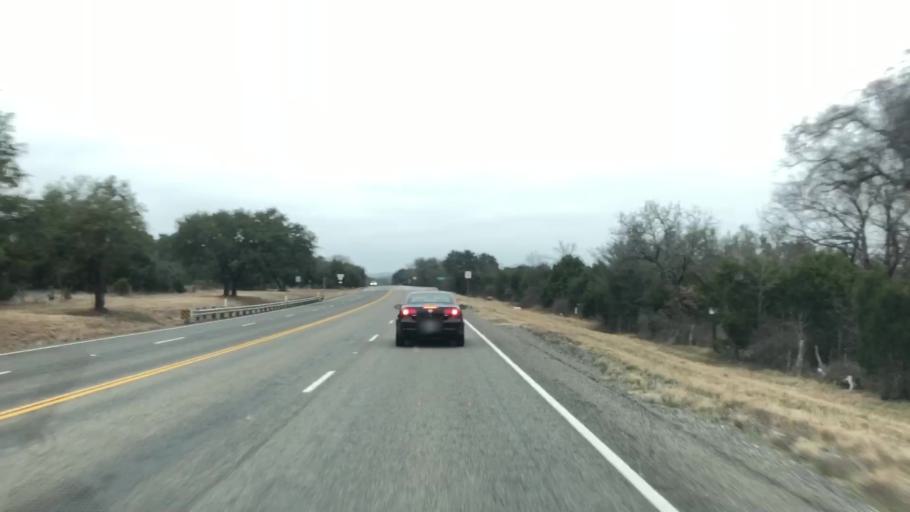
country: US
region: Texas
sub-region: Lampasas County
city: Lampasas
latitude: 31.0303
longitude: -98.1823
